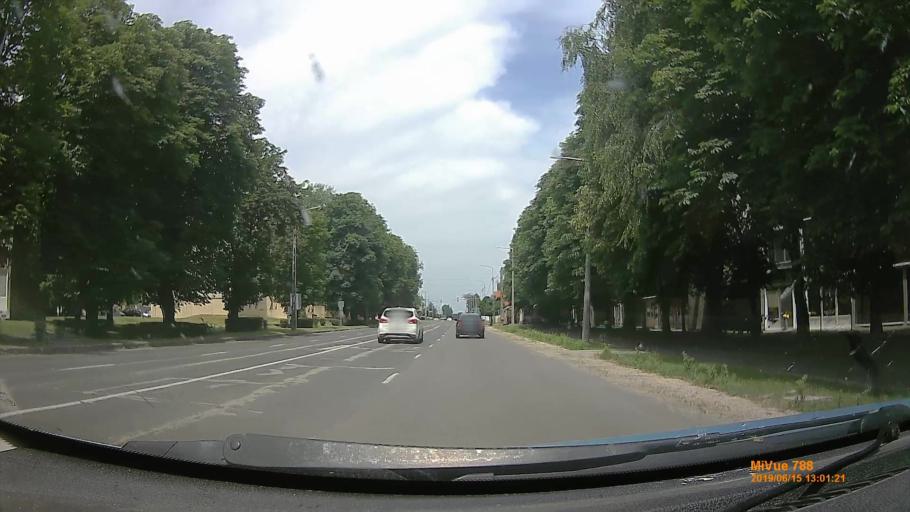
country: HU
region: Tolna
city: Dombovar
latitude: 46.3789
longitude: 18.1310
